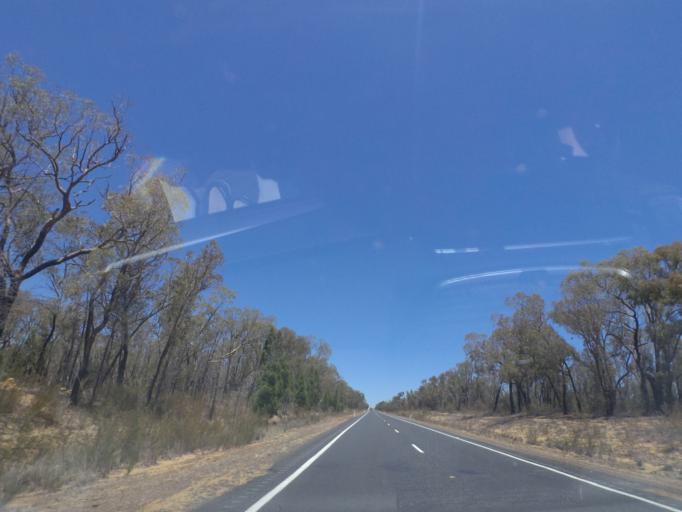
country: AU
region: New South Wales
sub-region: Warrumbungle Shire
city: Coonabarabran
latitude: -30.9520
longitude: 149.4212
